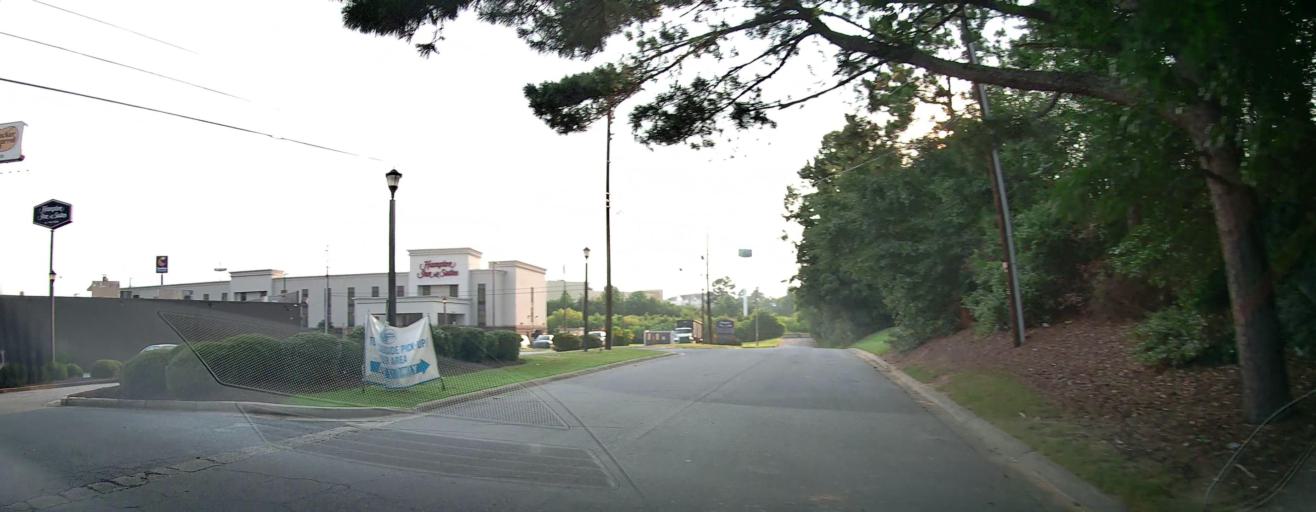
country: US
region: Georgia
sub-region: Bibb County
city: West Point
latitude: 32.8140
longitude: -83.7208
